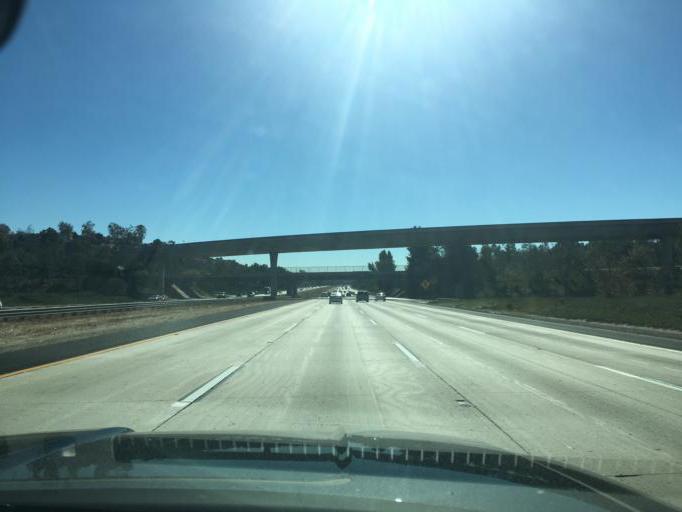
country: US
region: California
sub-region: San Diego County
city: La Mesa
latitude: 32.8252
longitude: -117.1172
